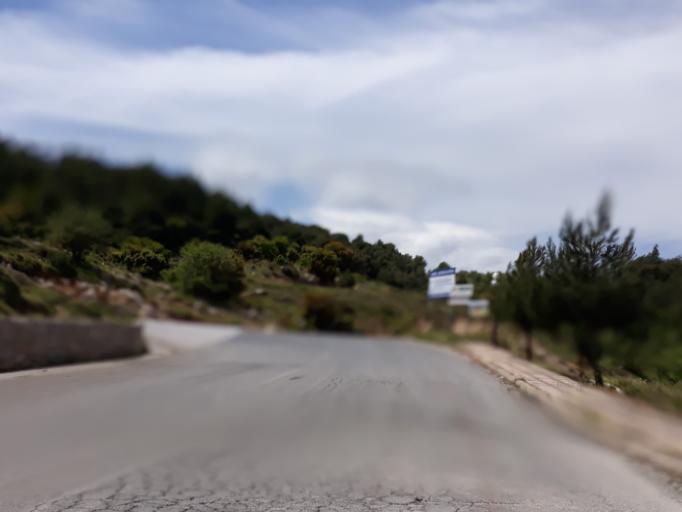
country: GR
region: Attica
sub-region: Nomarchia Dytikis Attikis
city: Magoula
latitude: 38.1723
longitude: 23.5458
